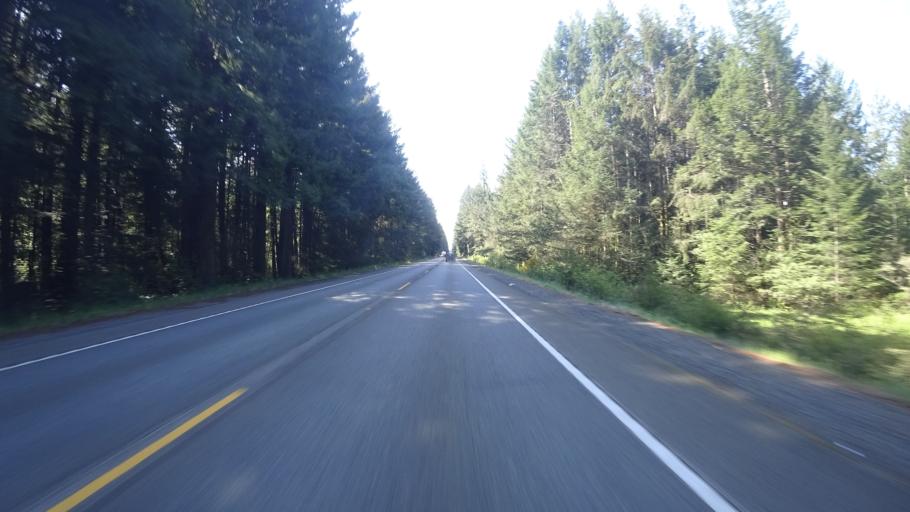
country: US
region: California
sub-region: Del Norte County
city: Bertsch-Oceanview
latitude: 41.8245
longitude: -124.1452
